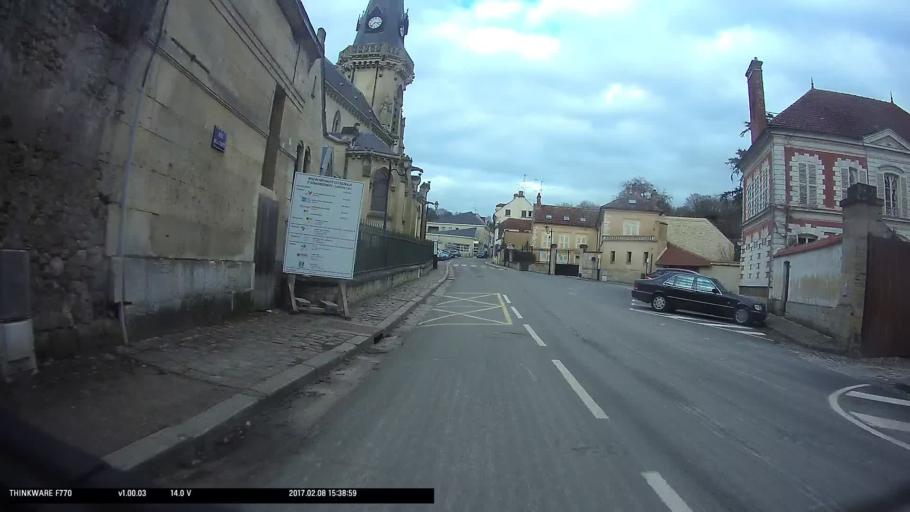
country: FR
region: Ile-de-France
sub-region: Departement du Val-d'Oise
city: Vigny
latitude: 49.0763
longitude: 1.9270
